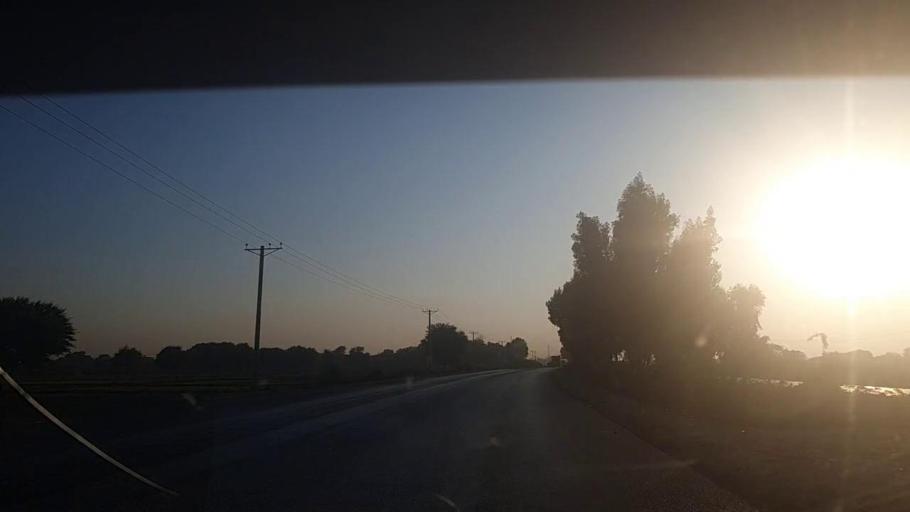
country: PK
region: Sindh
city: Hingorja
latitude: 27.1807
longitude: 68.3997
